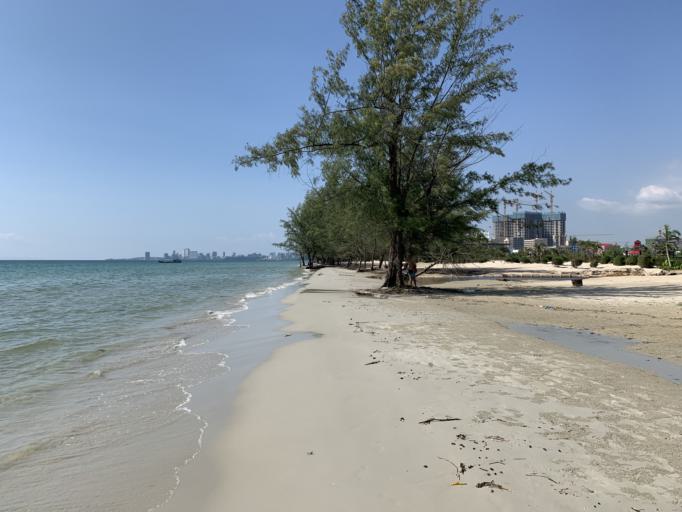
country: KH
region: Preah Sihanouk
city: Sihanoukville
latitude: 10.5629
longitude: 103.5566
